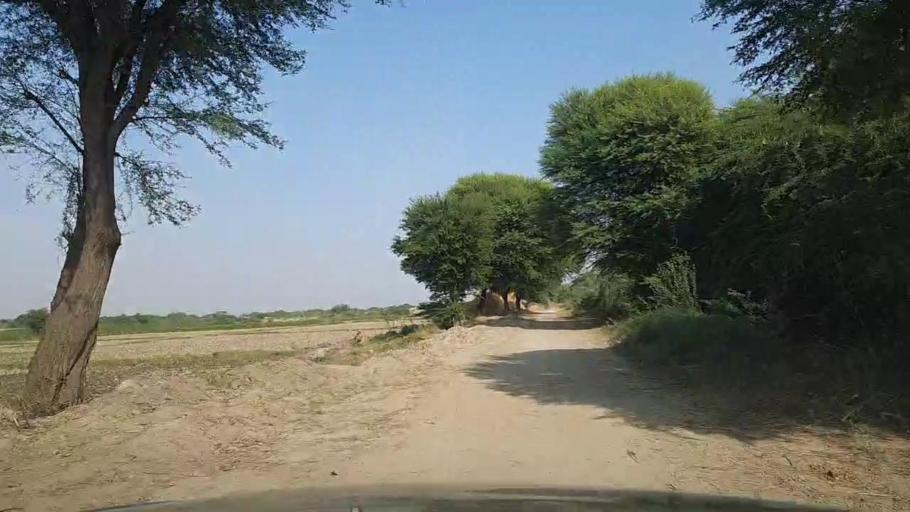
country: PK
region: Sindh
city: Thatta
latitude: 24.8006
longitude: 67.8277
